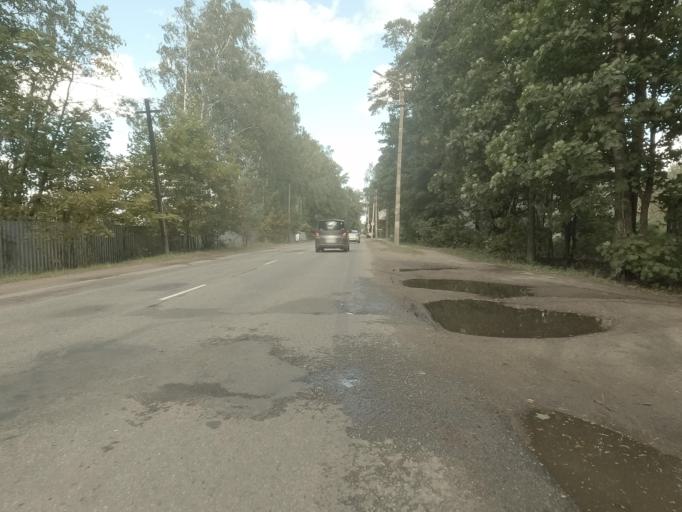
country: RU
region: Leningrad
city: Vsevolozhsk
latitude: 60.0166
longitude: 30.6755
